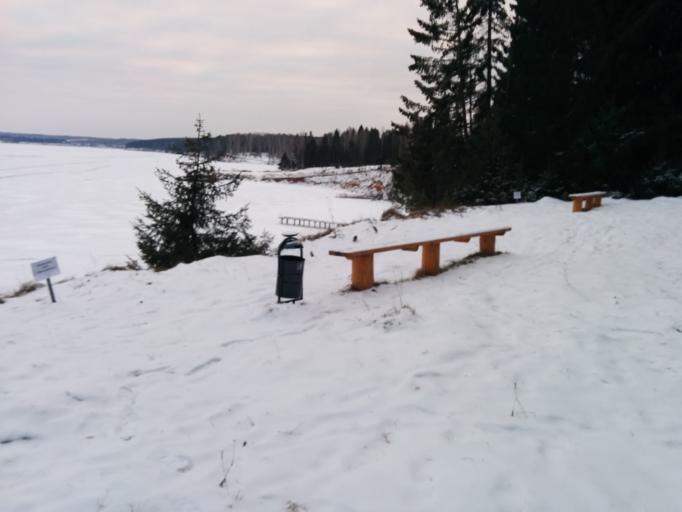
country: RU
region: Perm
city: Osa
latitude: 57.4591
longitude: 55.4732
